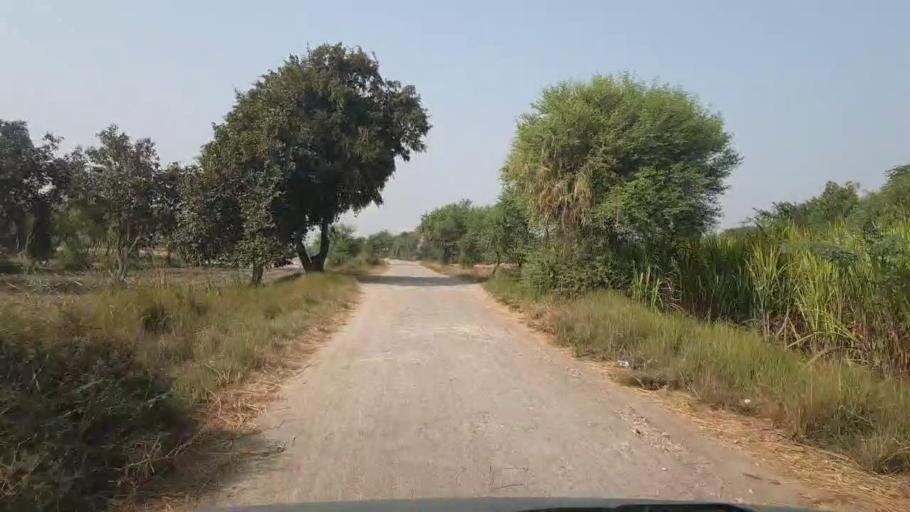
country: PK
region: Sindh
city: Tando Muhammad Khan
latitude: 25.0825
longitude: 68.3421
